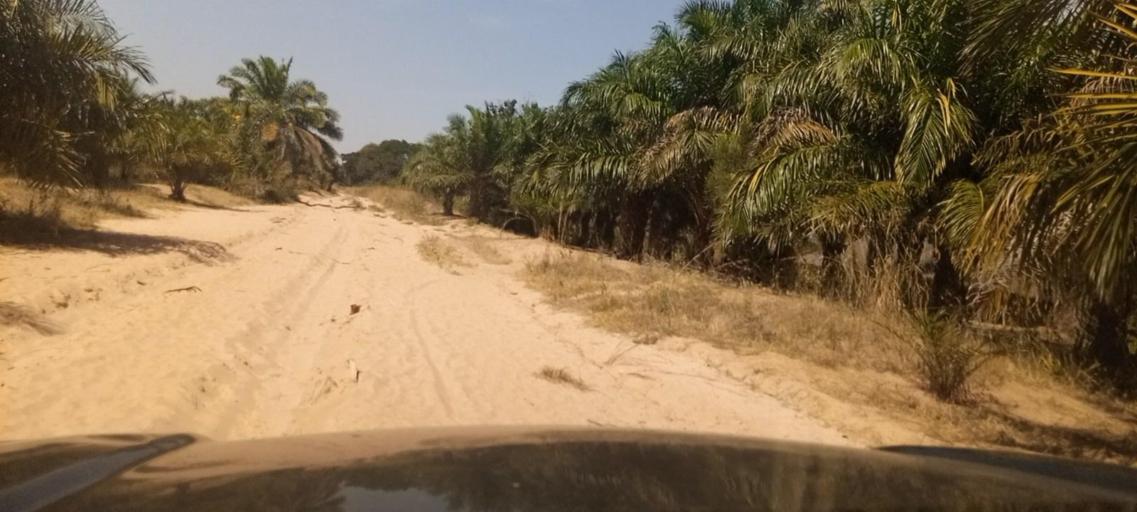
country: CD
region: Kasai-Oriental
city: Kabinda
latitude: -5.8038
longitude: 25.0152
